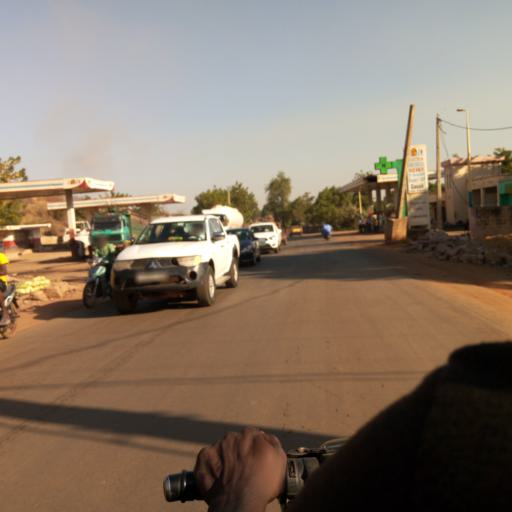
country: ML
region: Bamako
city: Bamako
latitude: 12.6603
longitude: -8.0342
